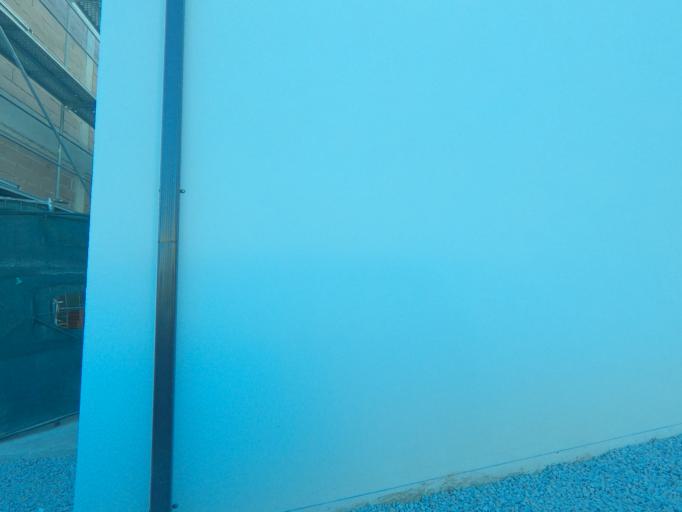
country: PT
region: Vila Real
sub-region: Peso da Regua
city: Godim
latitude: 41.1637
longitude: -7.8202
